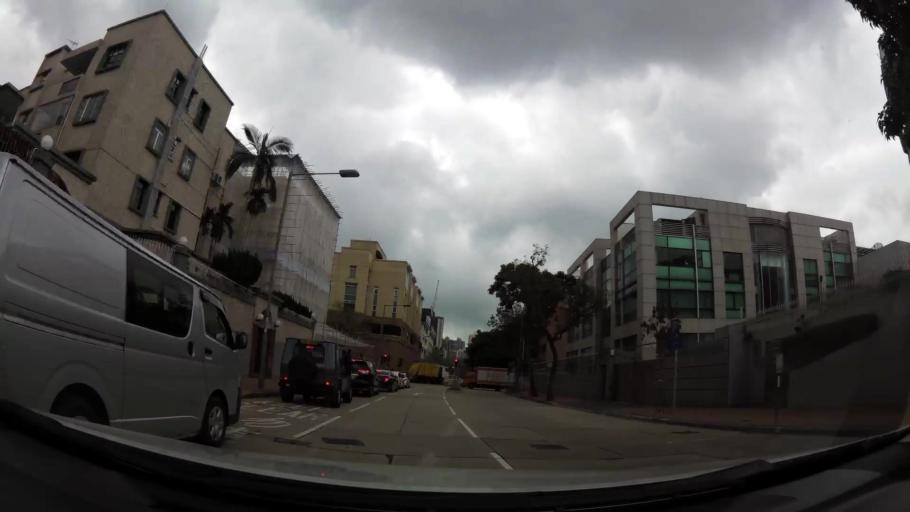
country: HK
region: Kowloon City
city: Kowloon
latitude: 22.3308
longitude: 114.1821
